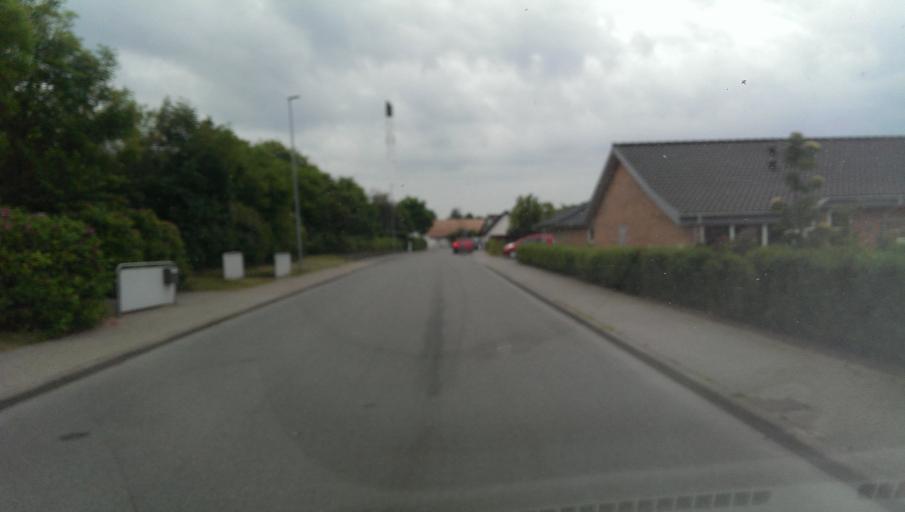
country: DK
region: South Denmark
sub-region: Esbjerg Kommune
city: Tjaereborg
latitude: 55.4651
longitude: 8.5746
